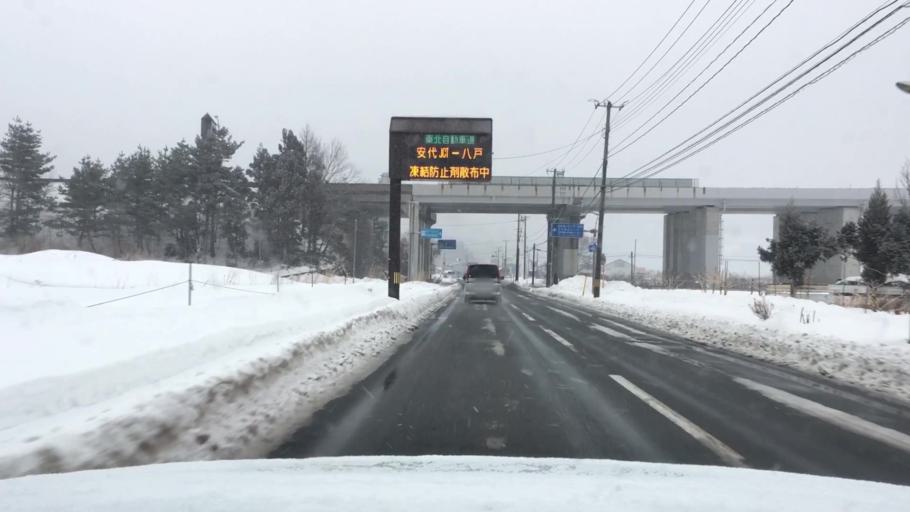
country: JP
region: Iwate
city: Ichinohe
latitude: 40.1082
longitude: 141.0513
